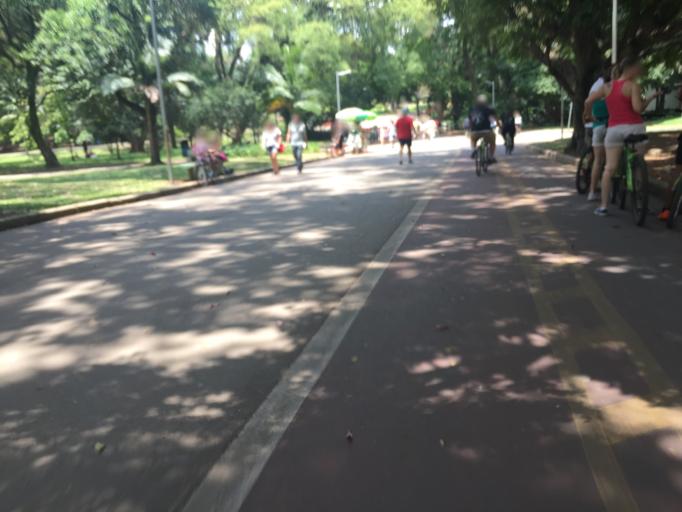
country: BR
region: Sao Paulo
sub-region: Sao Paulo
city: Sao Paulo
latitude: -23.5900
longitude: -46.6571
